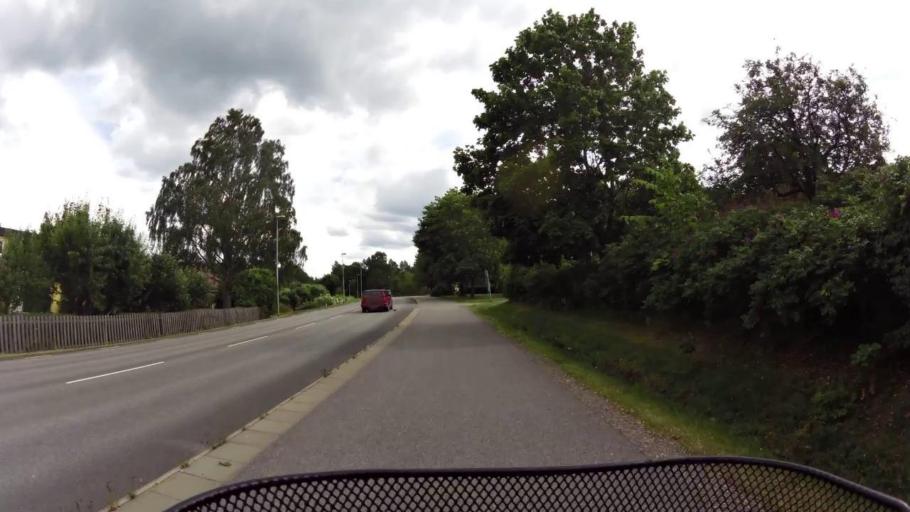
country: SE
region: OEstergoetland
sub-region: Linkopings Kommun
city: Malmslatt
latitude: 58.4139
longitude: 15.5219
